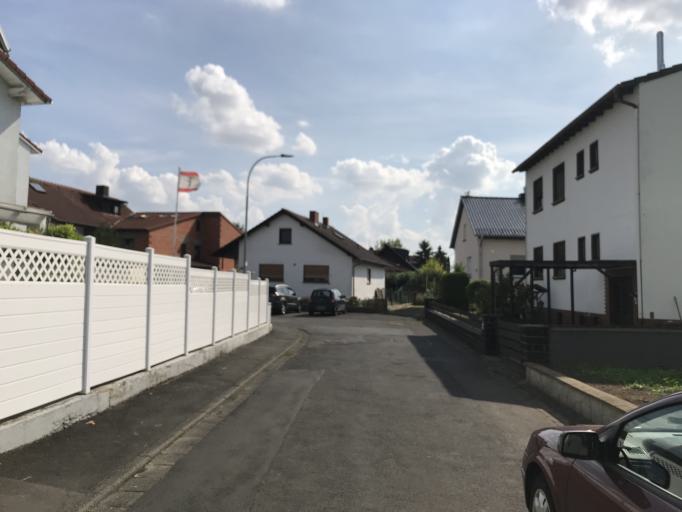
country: DE
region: Hesse
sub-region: Regierungsbezirk Darmstadt
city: Wolfersheim
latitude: 50.3777
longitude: 8.8069
